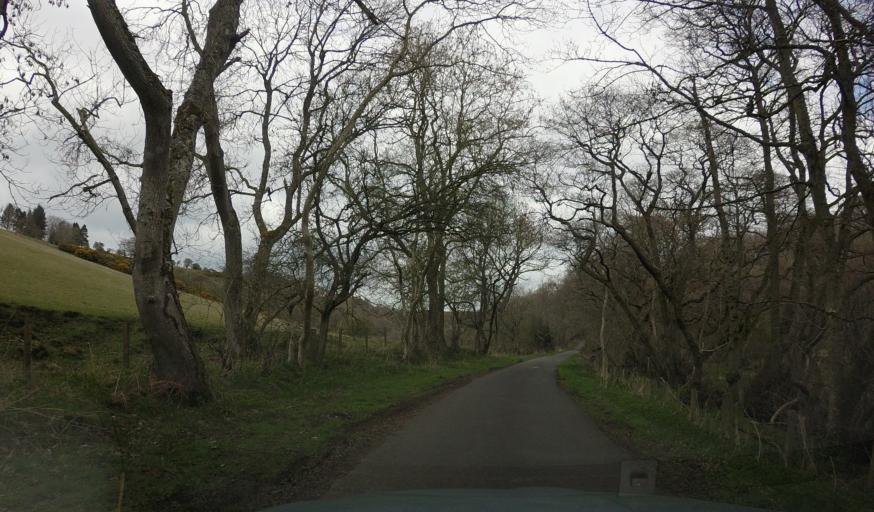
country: GB
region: Scotland
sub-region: Fife
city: Pathhead
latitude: 55.8437
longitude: -2.9945
